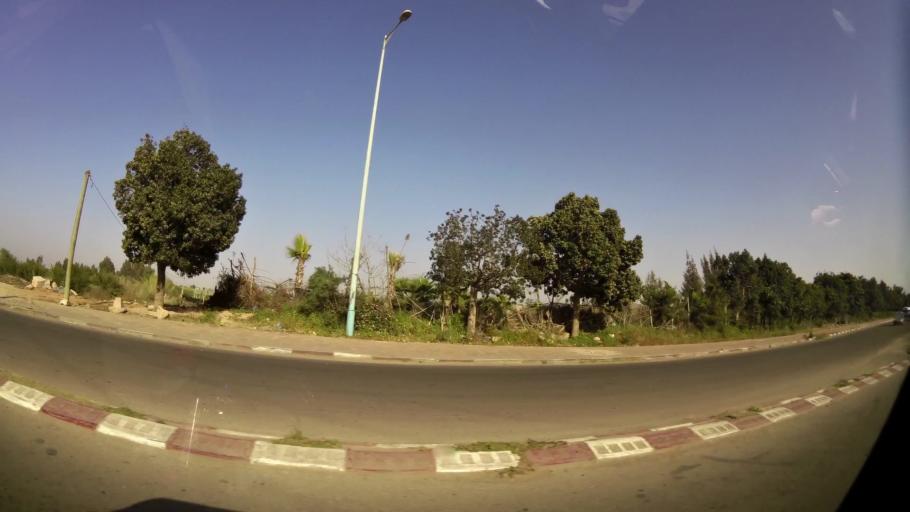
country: MA
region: Souss-Massa-Draa
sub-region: Inezgane-Ait Mellou
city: Inezgane
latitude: 30.3531
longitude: -9.5059
